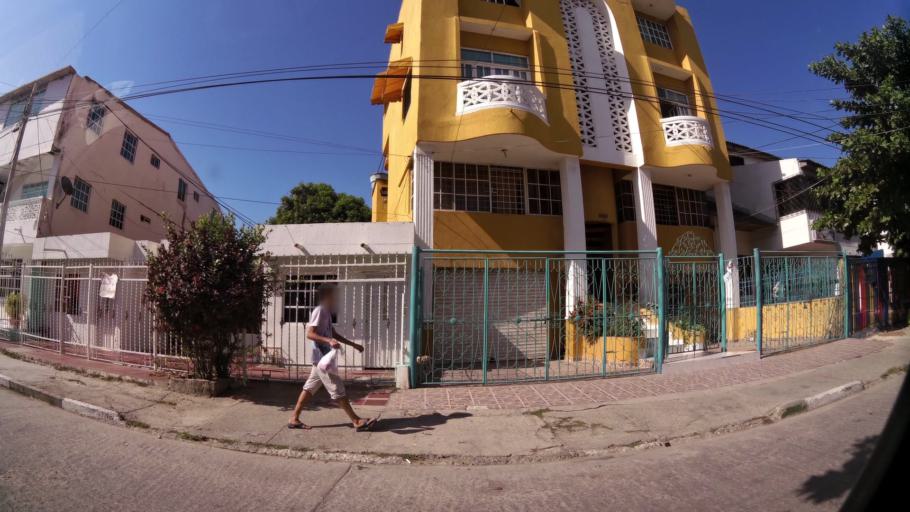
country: CO
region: Bolivar
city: Cartagena
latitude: 10.4299
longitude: -75.5345
